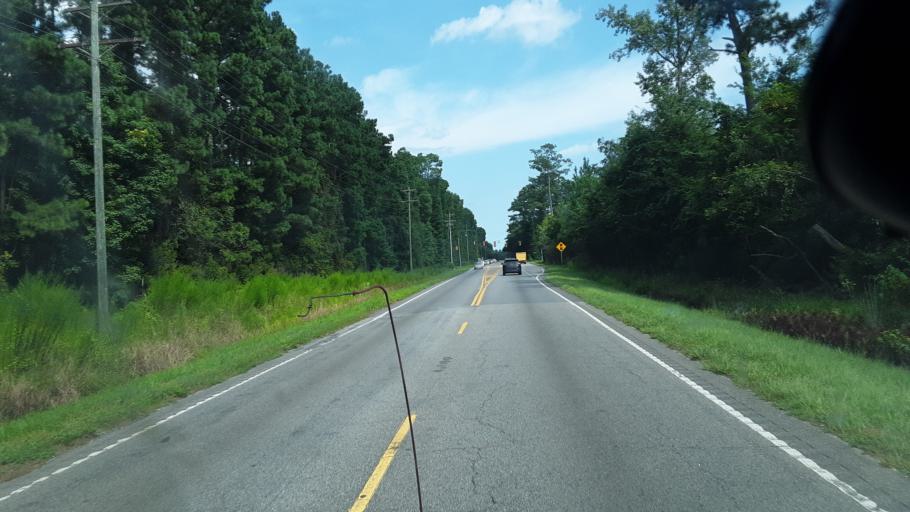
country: US
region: South Carolina
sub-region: Horry County
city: Red Hill
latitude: 33.8222
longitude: -78.9169
